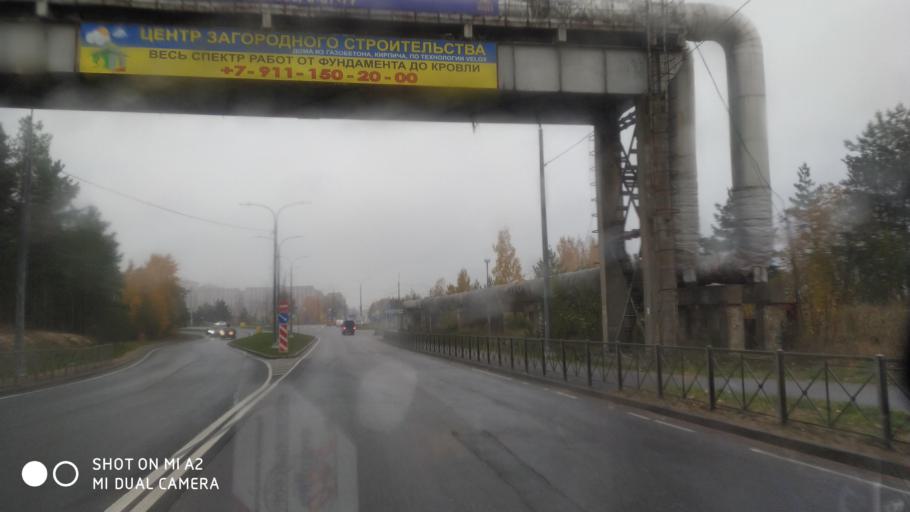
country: RU
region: Leningrad
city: Sosnovyy Bor
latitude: 59.8822
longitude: 29.0959
